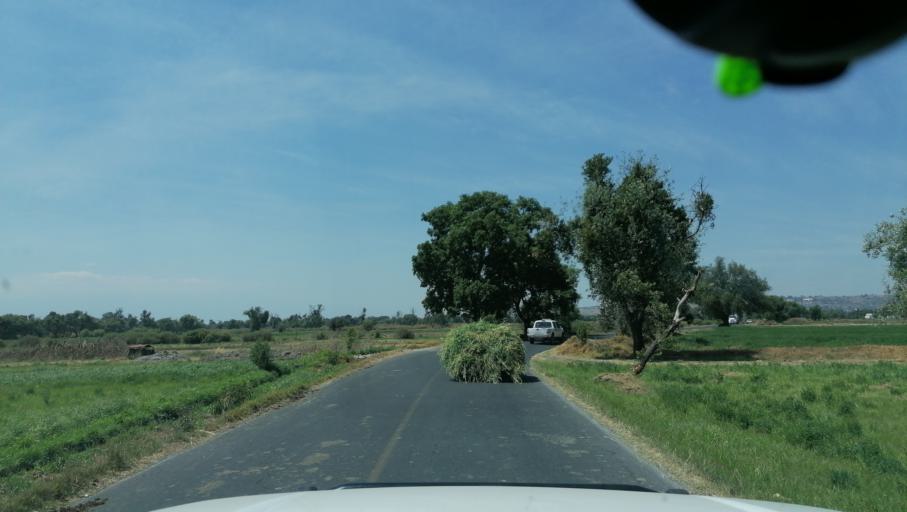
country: MX
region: Tlaxcala
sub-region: Tetlatlahuca
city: Tetlatlahuca
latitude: 19.2155
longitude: -98.2870
